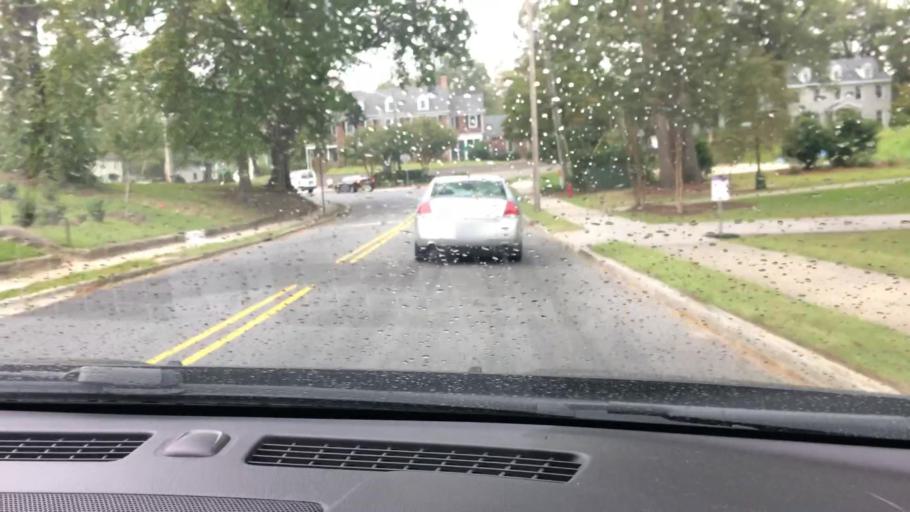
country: US
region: North Carolina
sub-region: Pitt County
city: Greenville
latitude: 35.6123
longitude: -77.3792
